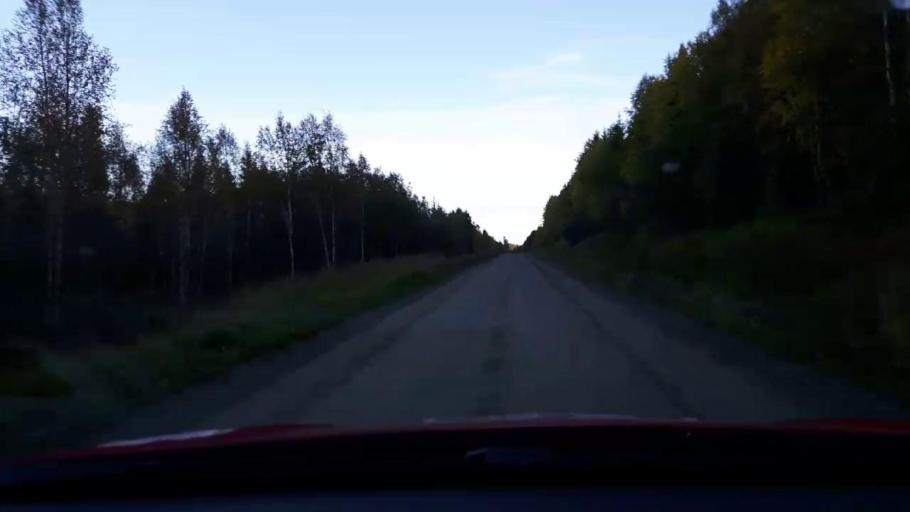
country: SE
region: Jaemtland
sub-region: OEstersunds Kommun
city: Brunflo
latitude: 62.9396
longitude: 14.9905
